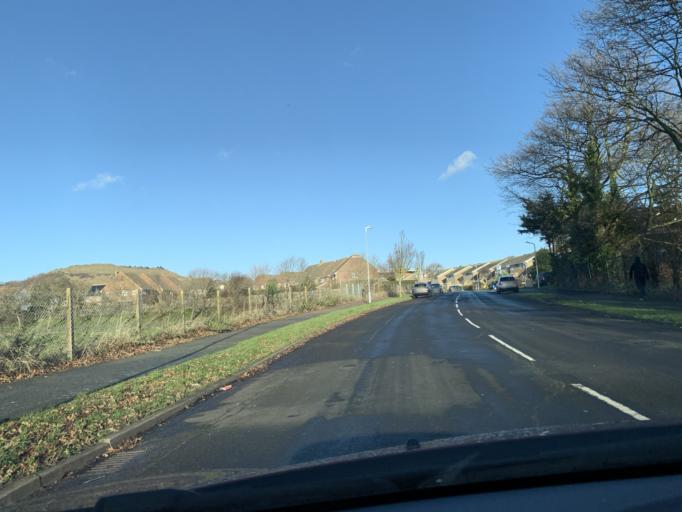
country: GB
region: England
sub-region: Kent
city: Folkestone
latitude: 51.0883
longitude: 1.1637
